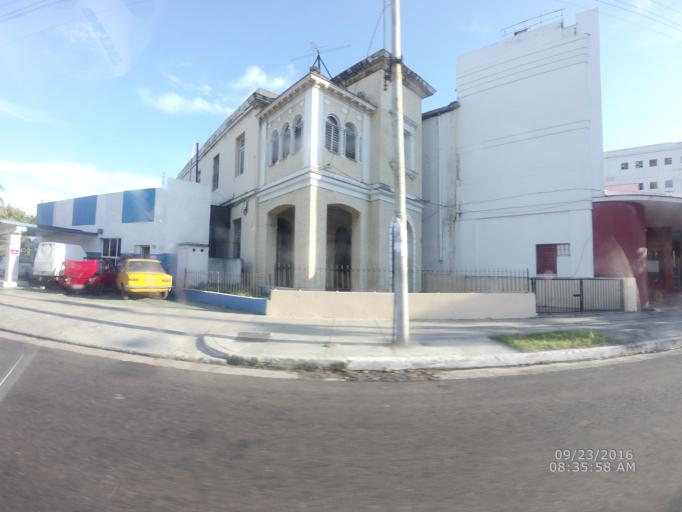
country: CU
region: La Habana
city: Havana
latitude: 23.1269
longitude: -82.4007
